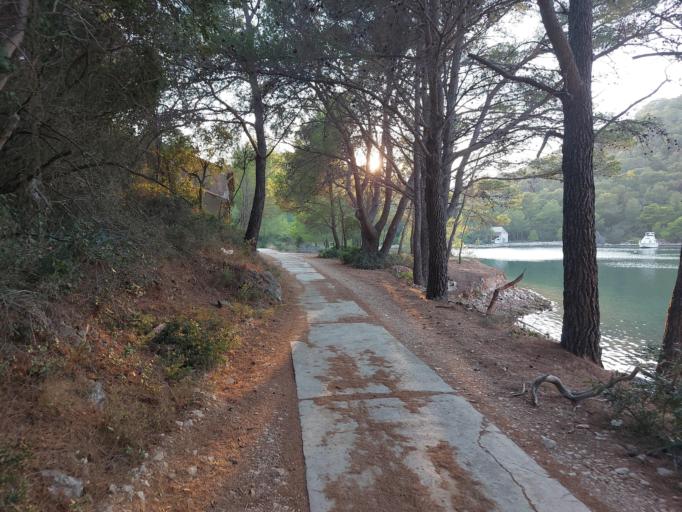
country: HR
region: Dubrovacko-Neretvanska
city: Smokvica
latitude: 42.7632
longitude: 16.8110
